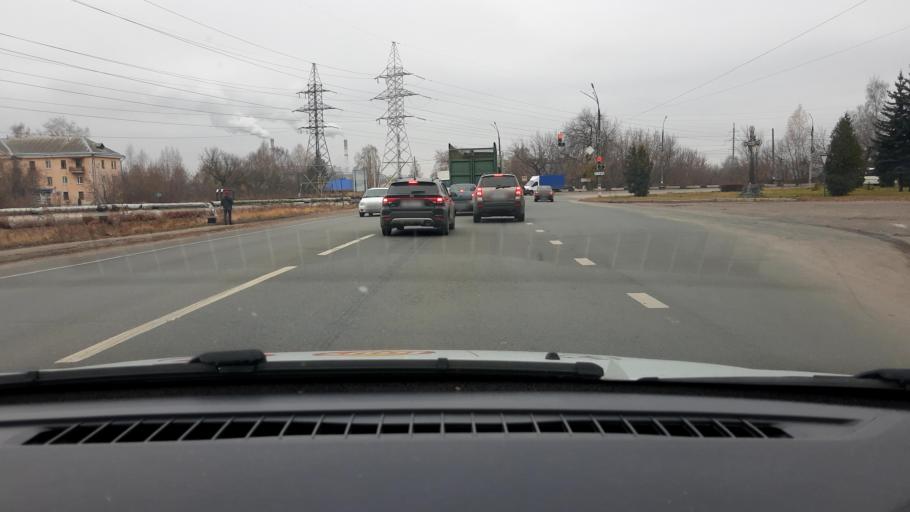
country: RU
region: Nizjnij Novgorod
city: Novaya Balakhna
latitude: 56.4867
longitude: 43.5974
